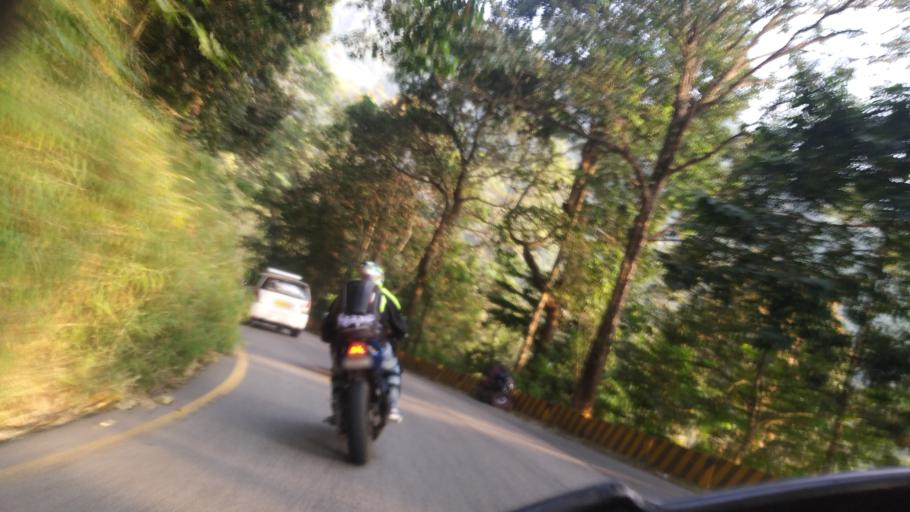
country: IN
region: Kerala
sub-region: Wayanad
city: Kalpetta
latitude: 11.5079
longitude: 76.0284
